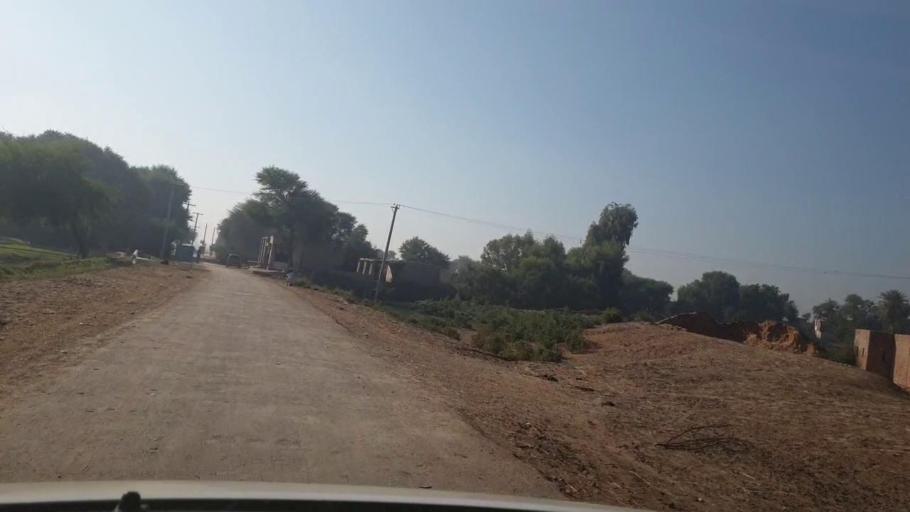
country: PK
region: Sindh
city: Dadu
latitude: 26.6498
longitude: 67.8221
